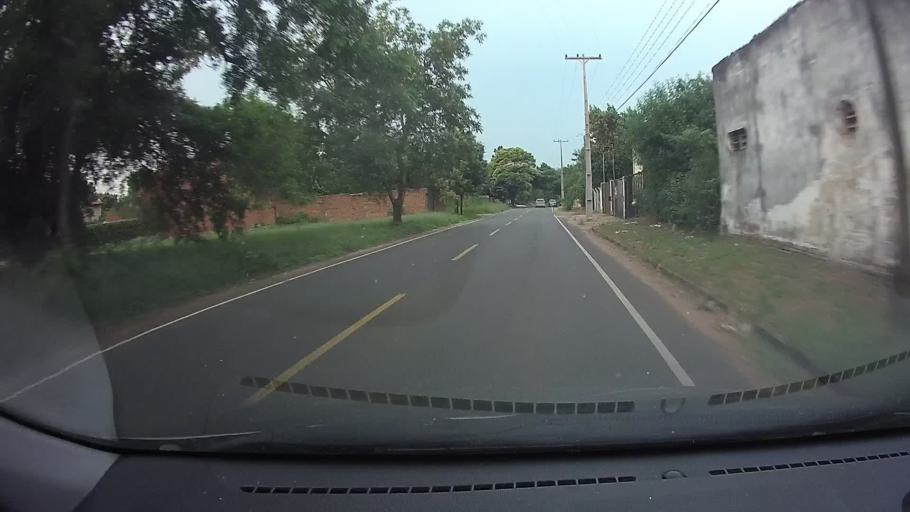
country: PY
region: Central
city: San Lorenzo
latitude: -25.2581
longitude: -57.5032
